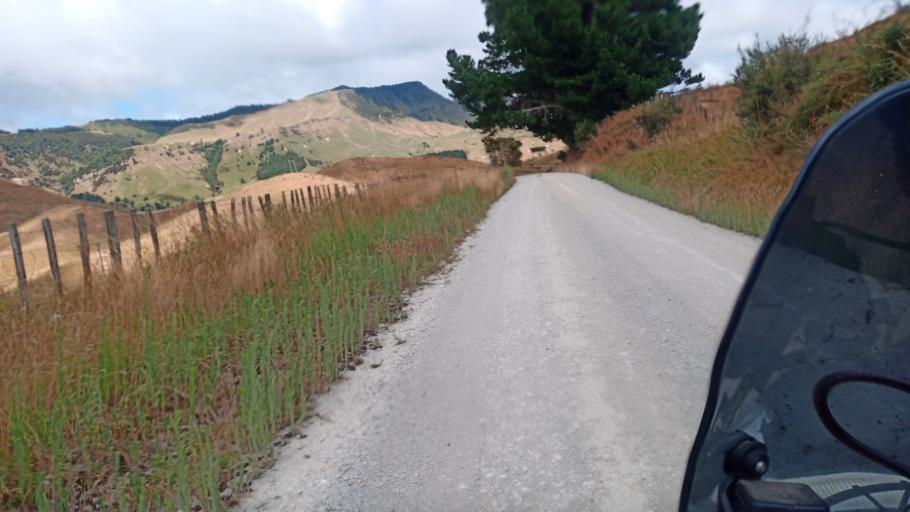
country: NZ
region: Hawke's Bay
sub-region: Wairoa District
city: Wairoa
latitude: -38.6114
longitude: 177.4377
